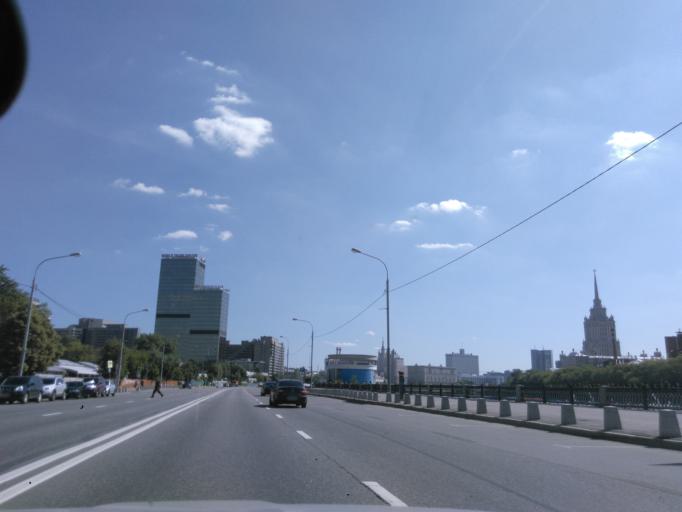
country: RU
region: Moskovskaya
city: Presnenskiy
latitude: 55.7505
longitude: 37.5496
